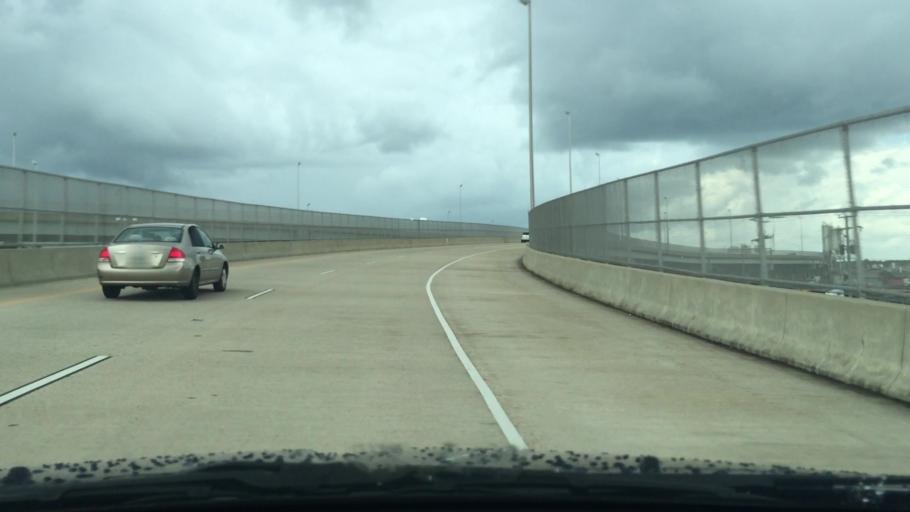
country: US
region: Virginia
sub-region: City of Portsmouth
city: Portsmouth
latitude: 36.8525
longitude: -76.3287
